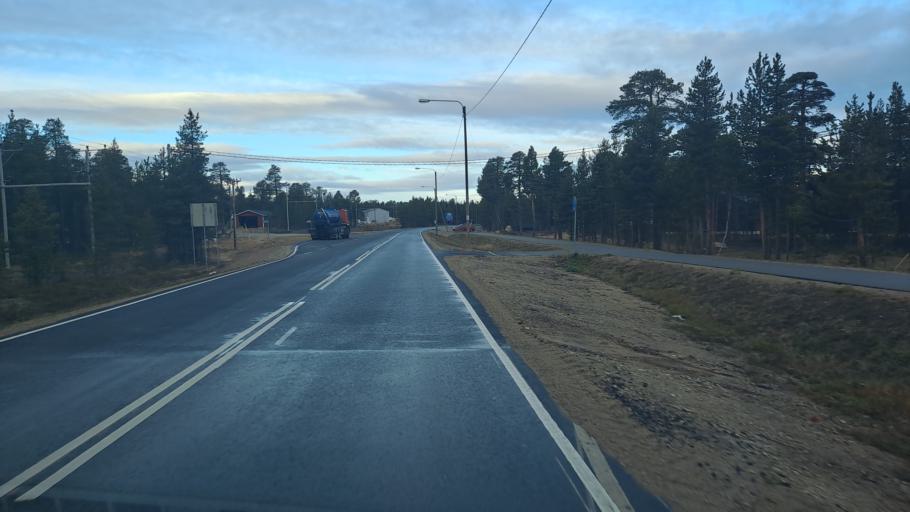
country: FI
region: Lapland
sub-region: Pohjois-Lappi
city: Inari
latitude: 68.8974
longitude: 27.0878
